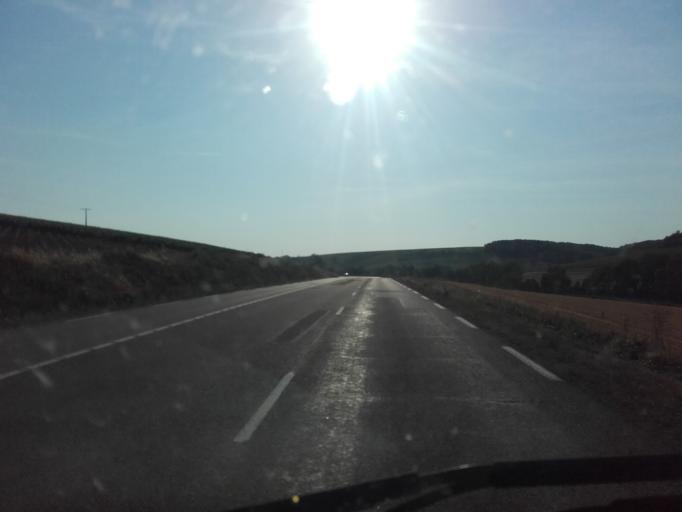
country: FR
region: Bourgogne
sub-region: Departement de l'Yonne
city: Chablis
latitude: 47.8234
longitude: 3.7590
